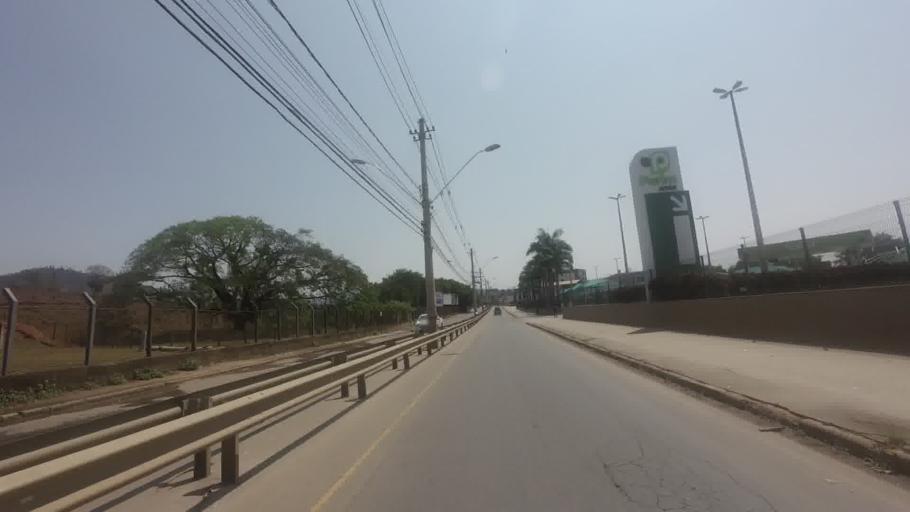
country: BR
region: Espirito Santo
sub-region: Cachoeiro De Itapemirim
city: Cachoeiro de Itapemirim
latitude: -20.8436
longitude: -41.1569
